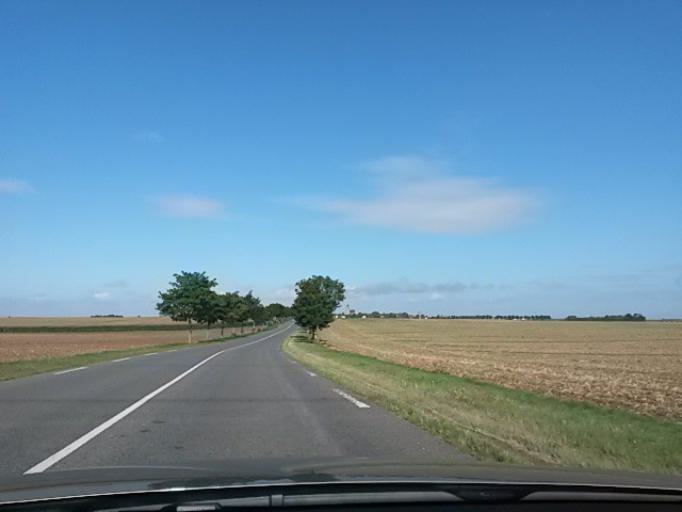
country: FR
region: Centre
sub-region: Departement d'Eure-et-Loir
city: Janville
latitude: 48.1923
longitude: 1.9051
